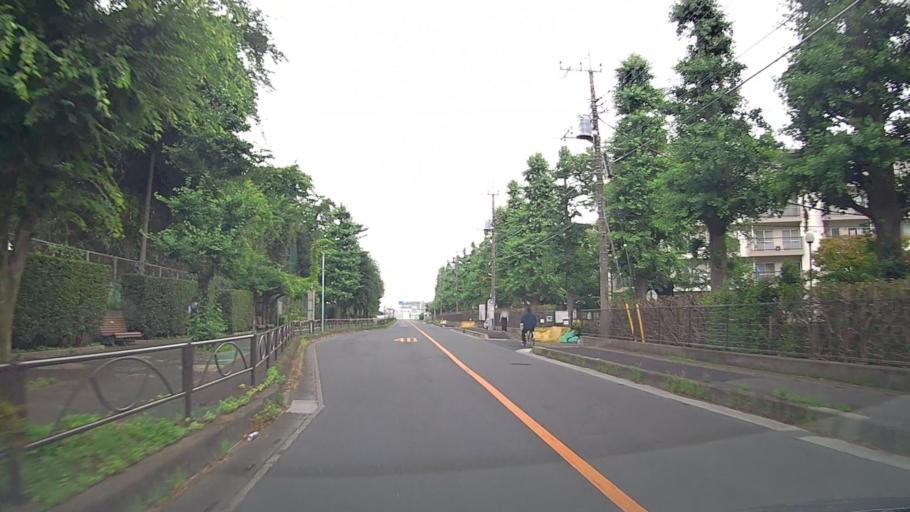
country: JP
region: Saitama
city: Wako
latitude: 35.7739
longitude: 139.6165
